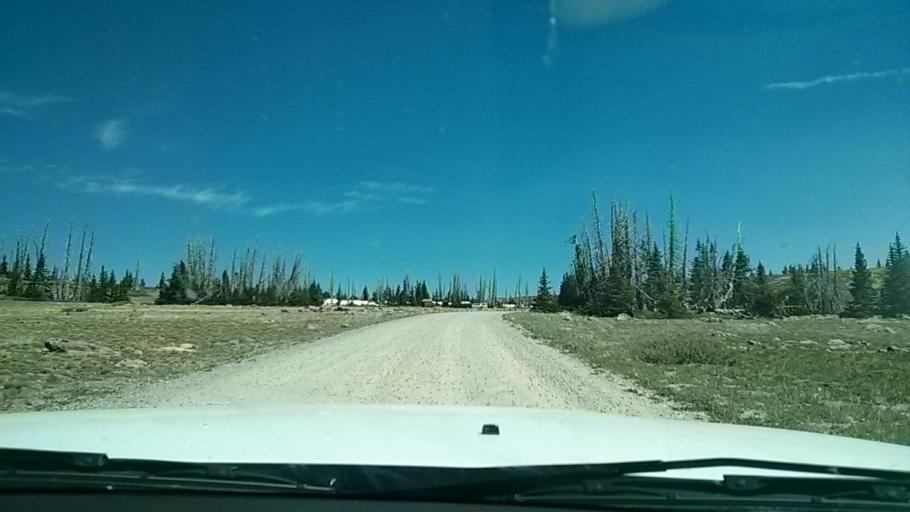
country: US
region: Utah
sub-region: Iron County
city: Parowan
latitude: 37.6842
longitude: -112.8196
